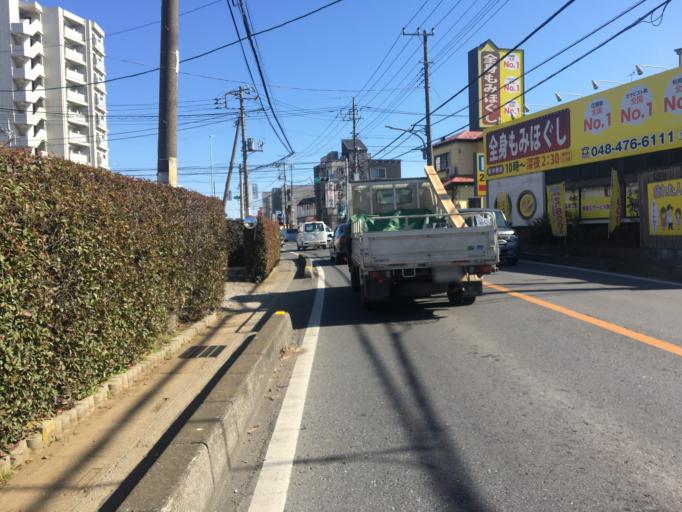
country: JP
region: Saitama
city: Shiki
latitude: 35.8226
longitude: 139.5861
